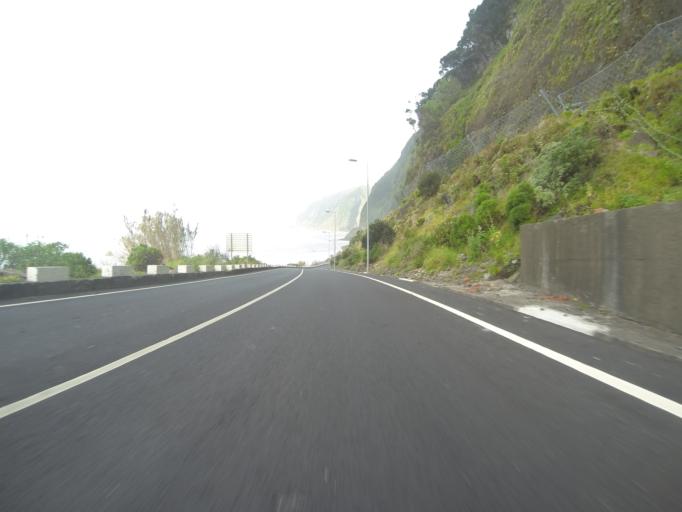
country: PT
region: Madeira
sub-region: Sao Vicente
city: Sao Vicente
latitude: 32.8157
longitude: -17.0824
